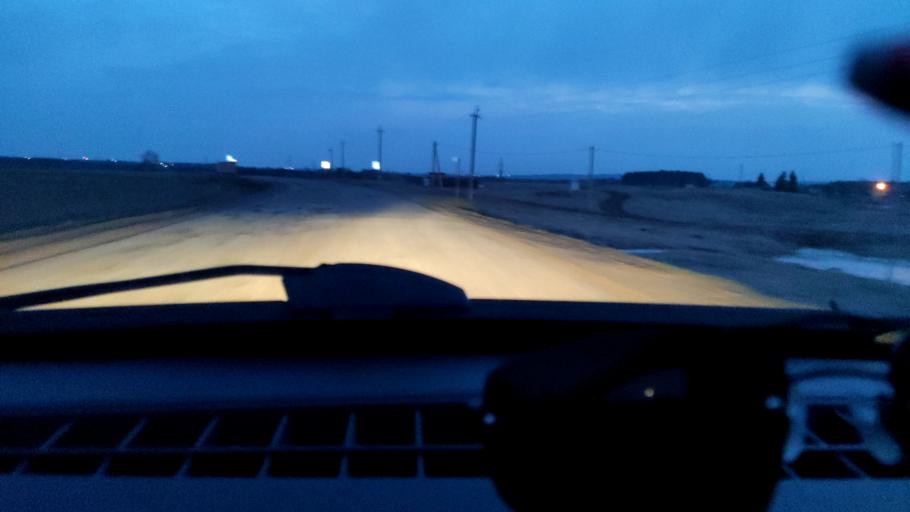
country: RU
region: Bashkortostan
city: Kabakovo
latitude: 54.4987
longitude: 56.1780
